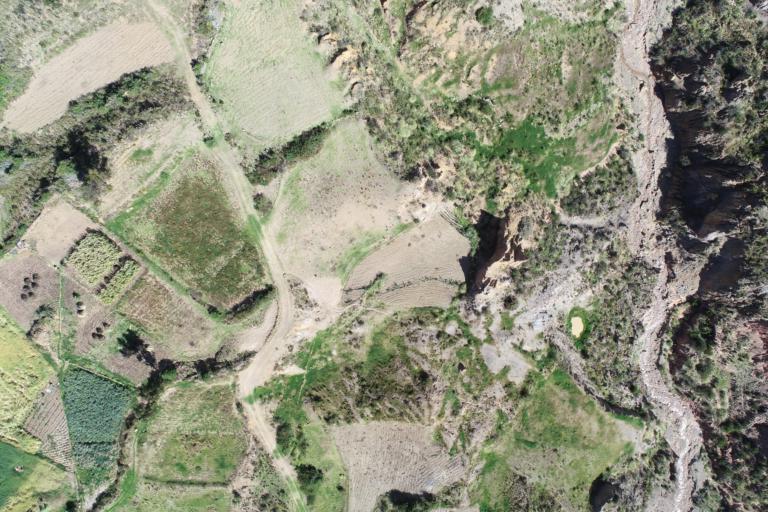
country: BO
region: La Paz
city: La Paz
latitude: -16.5565
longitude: -67.9902
